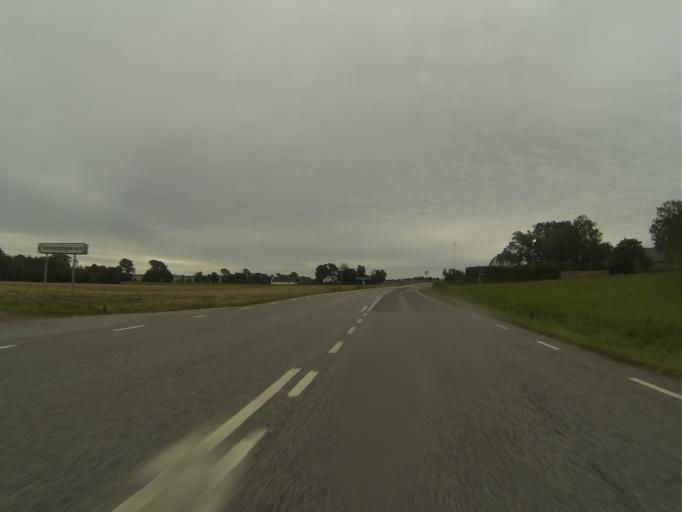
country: SE
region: Skane
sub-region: Svedala Kommun
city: Klagerup
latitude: 55.6339
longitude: 13.2867
